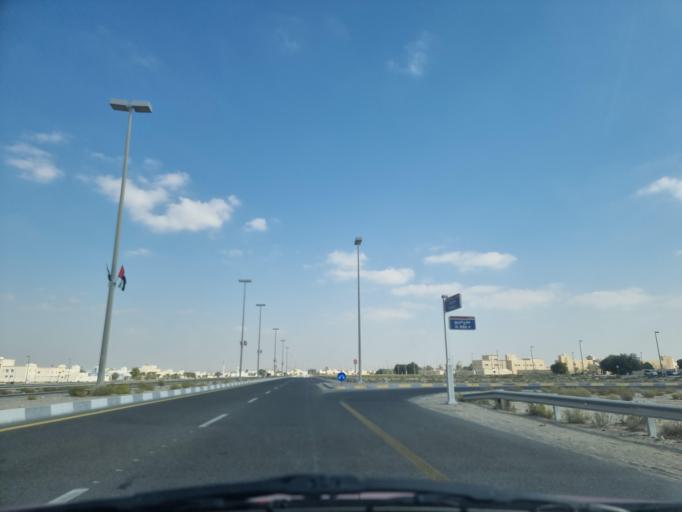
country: AE
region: Abu Dhabi
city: Abu Dhabi
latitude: 24.4037
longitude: 54.7379
